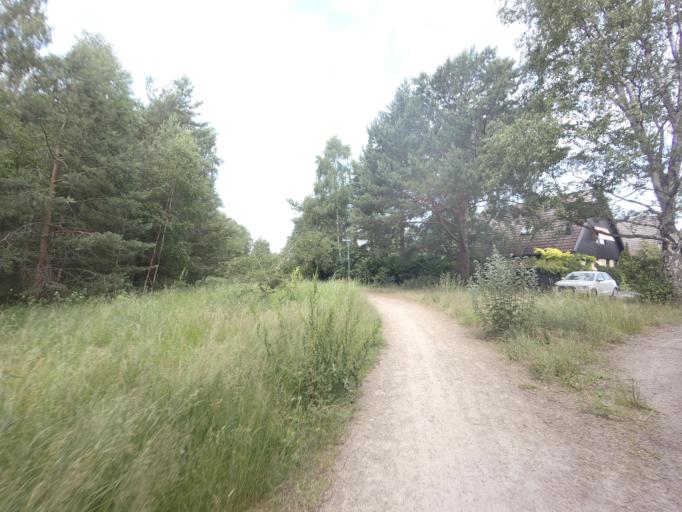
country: SE
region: Skane
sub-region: Vellinge Kommun
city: Skanor med Falsterbo
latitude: 55.4028
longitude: 12.8608
